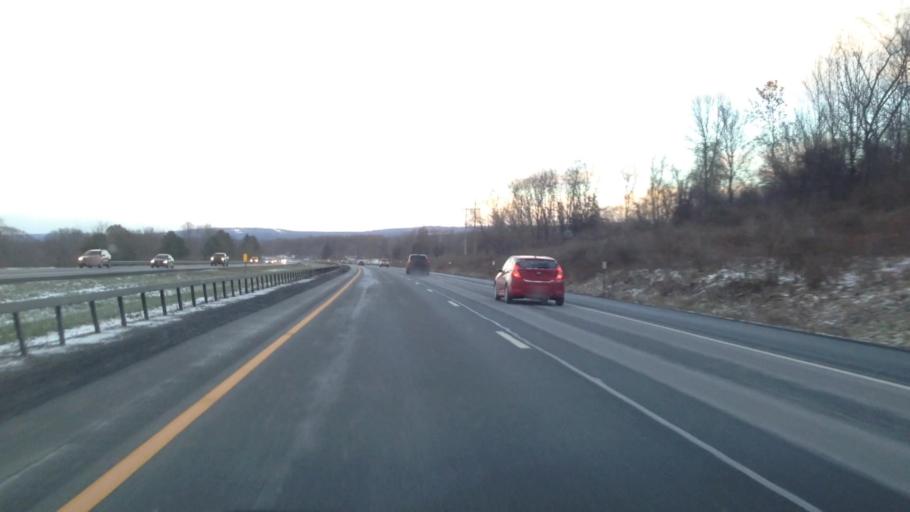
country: US
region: New York
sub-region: Herkimer County
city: Frankfort
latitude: 43.0487
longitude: -75.0595
